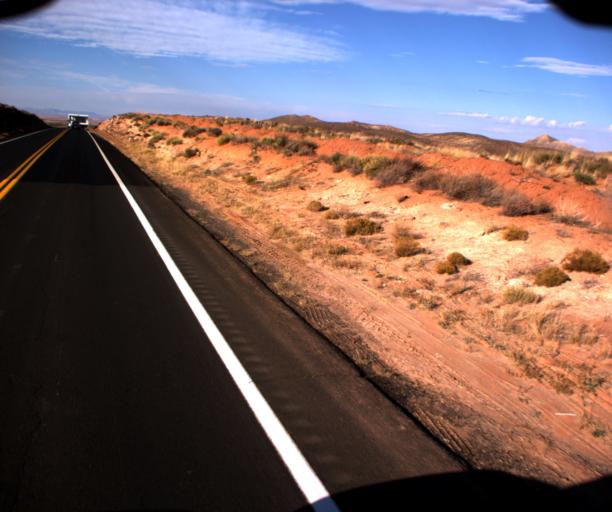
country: US
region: Arizona
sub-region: Apache County
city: Lukachukai
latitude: 36.9522
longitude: -109.5136
